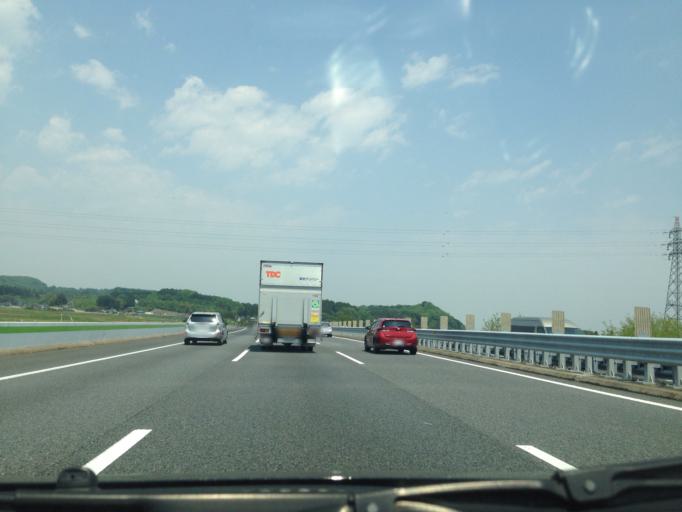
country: JP
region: Tochigi
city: Kanuma
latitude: 36.4842
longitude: 139.7351
